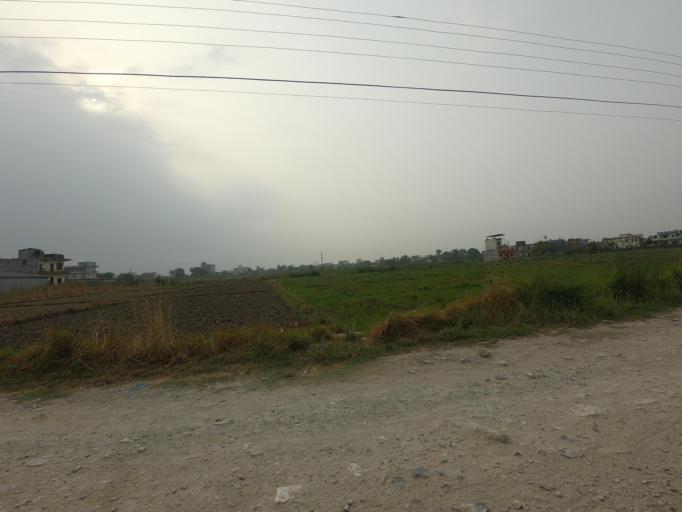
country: NP
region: Western Region
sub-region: Lumbini Zone
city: Bhairahawa
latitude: 27.5274
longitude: 83.4512
